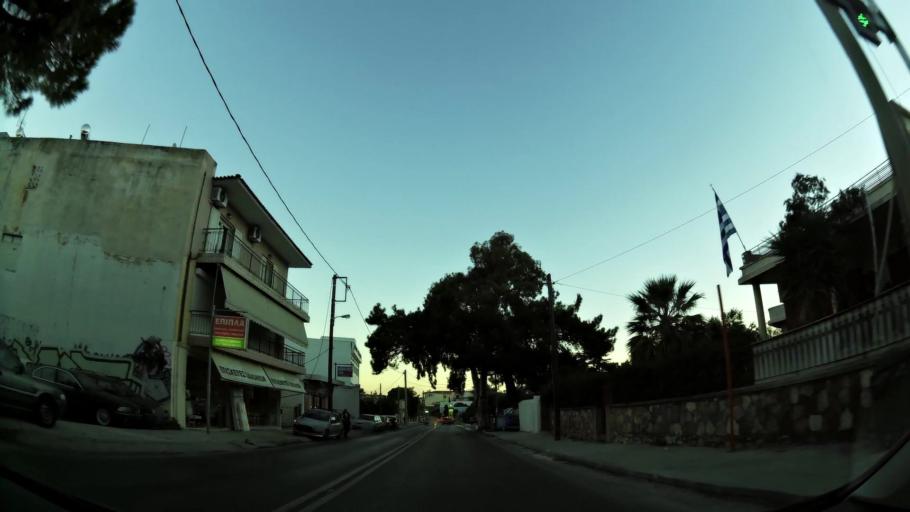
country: GR
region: Attica
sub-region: Nomarchia Anatolikis Attikis
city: Paiania
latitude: 37.9586
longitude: 23.8569
